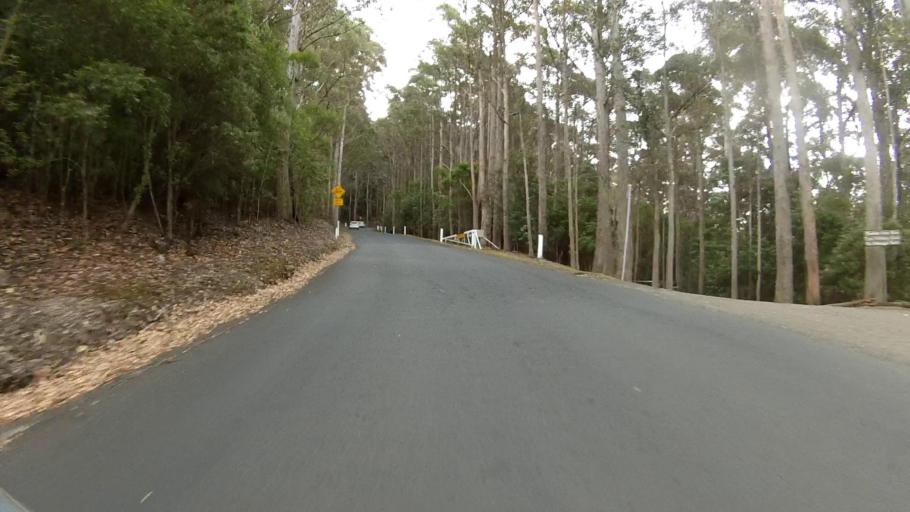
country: AU
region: Tasmania
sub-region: Hobart
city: Dynnyrne
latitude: -42.9168
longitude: 147.2612
